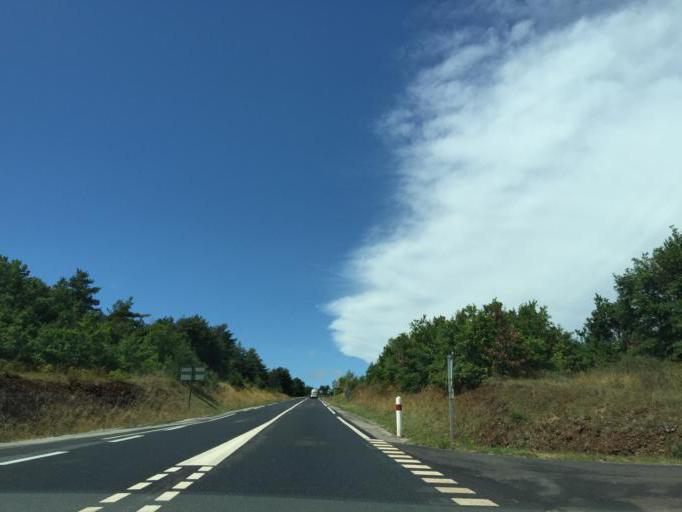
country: FR
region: Midi-Pyrenees
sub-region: Departement de l'Aveyron
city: Millau
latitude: 44.1802
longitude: 3.0329
